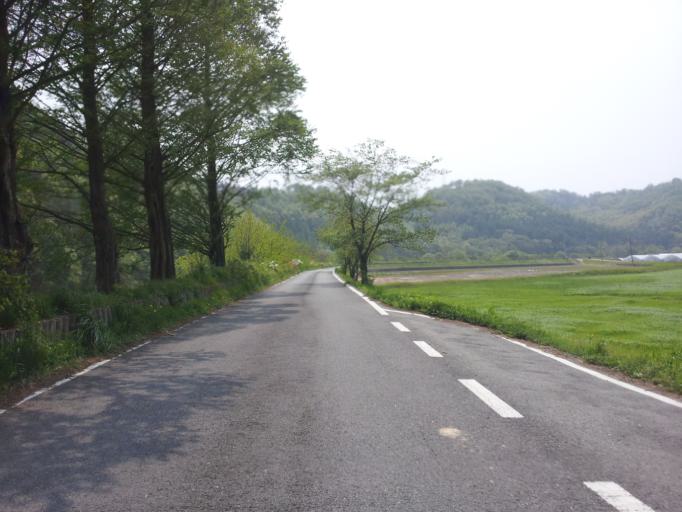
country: KR
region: Daejeon
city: Daejeon
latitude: 36.2600
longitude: 127.2942
